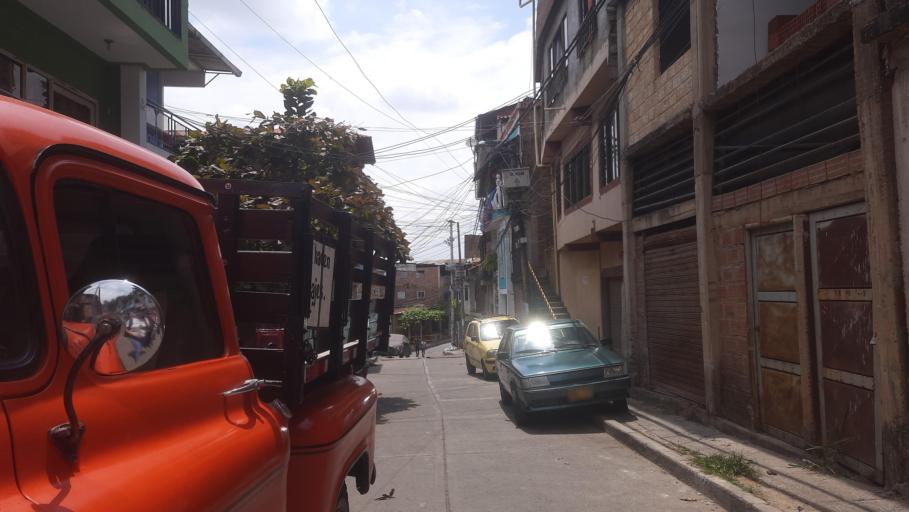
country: CO
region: Valle del Cauca
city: Cali
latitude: 3.3738
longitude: -76.5561
